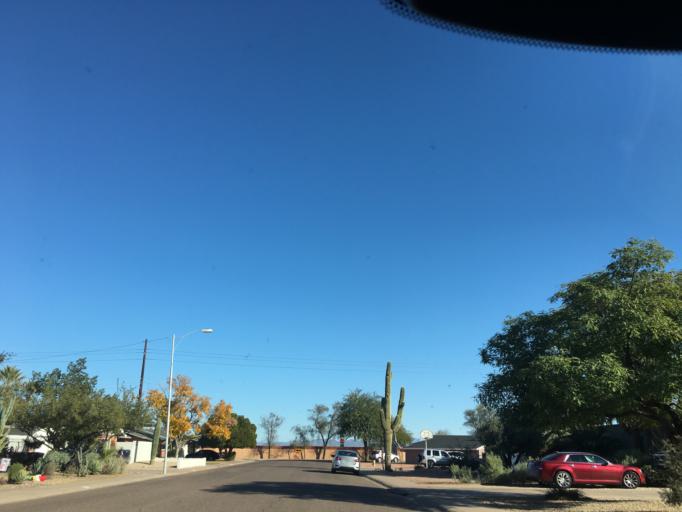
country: US
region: Arizona
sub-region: Maricopa County
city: Scottsdale
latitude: 33.5057
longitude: -111.8930
